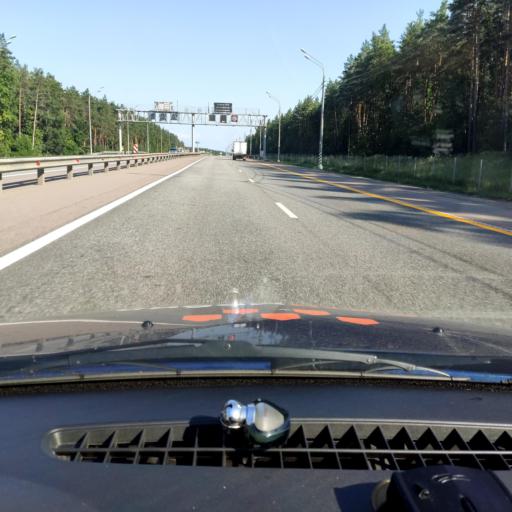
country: RU
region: Lipetsk
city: Zadonsk
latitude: 52.3220
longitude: 39.0312
